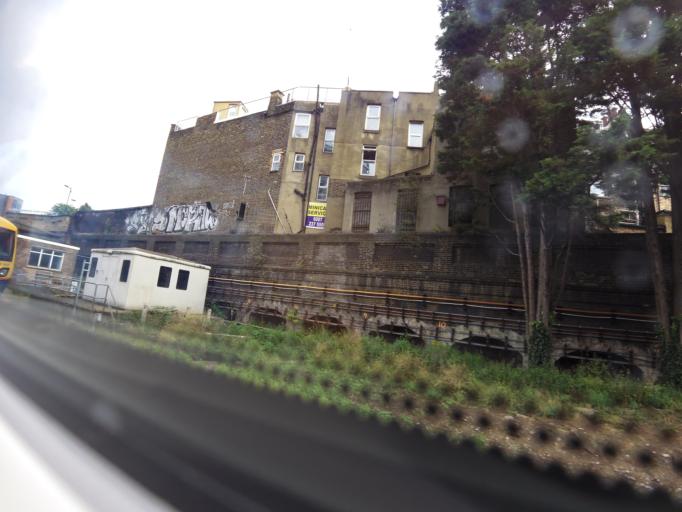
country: GB
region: England
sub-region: Greater London
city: Poplar
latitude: 51.4930
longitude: -0.0469
